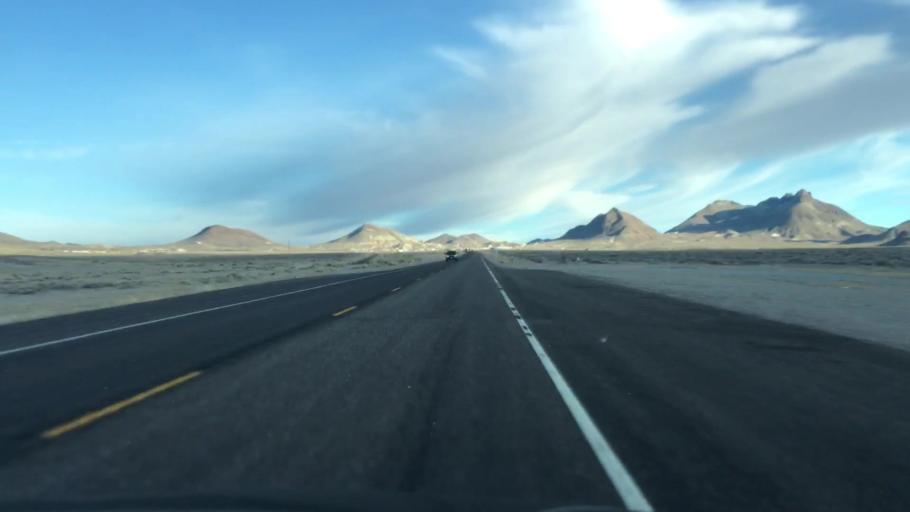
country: US
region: Nevada
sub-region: Nye County
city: Tonopah
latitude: 38.0856
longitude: -117.2832
